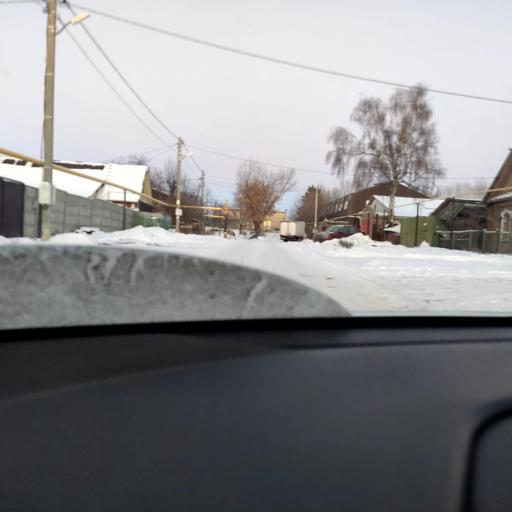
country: RU
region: Tatarstan
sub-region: Gorod Kazan'
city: Kazan
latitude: 55.7398
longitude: 49.0934
